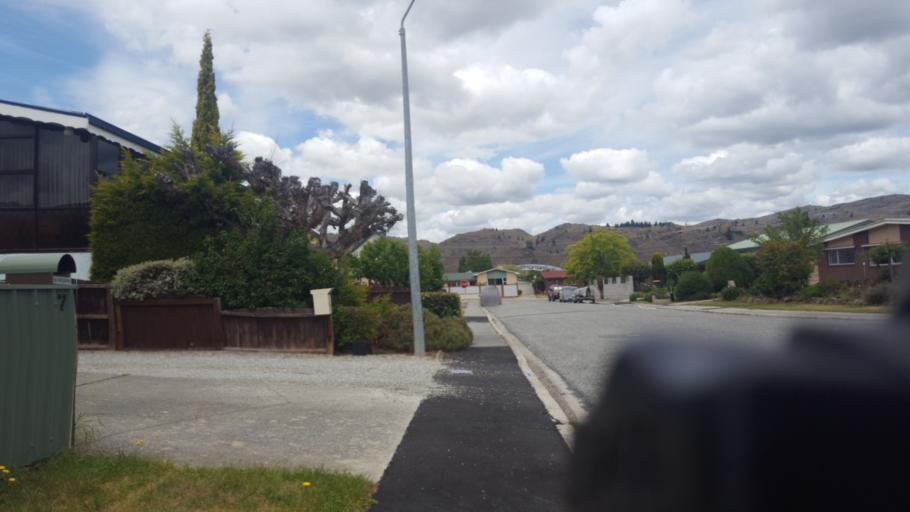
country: NZ
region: Otago
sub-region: Queenstown-Lakes District
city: Wanaka
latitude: -45.2545
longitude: 169.3864
